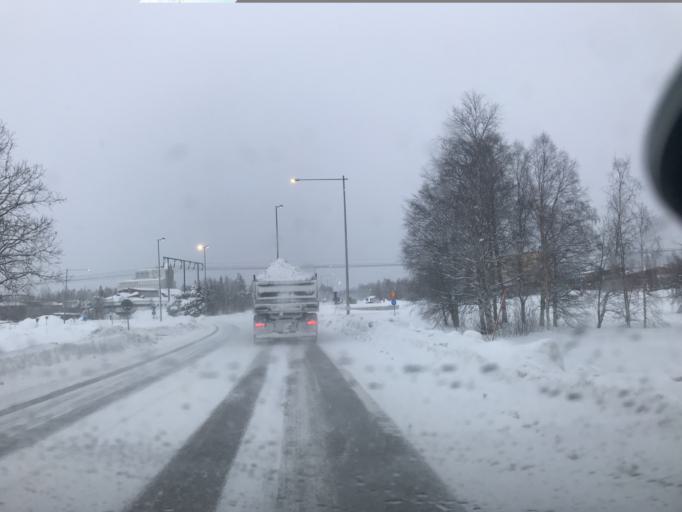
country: SE
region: Norrbotten
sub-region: Lulea Kommun
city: Lulea
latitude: 65.6145
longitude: 22.1330
